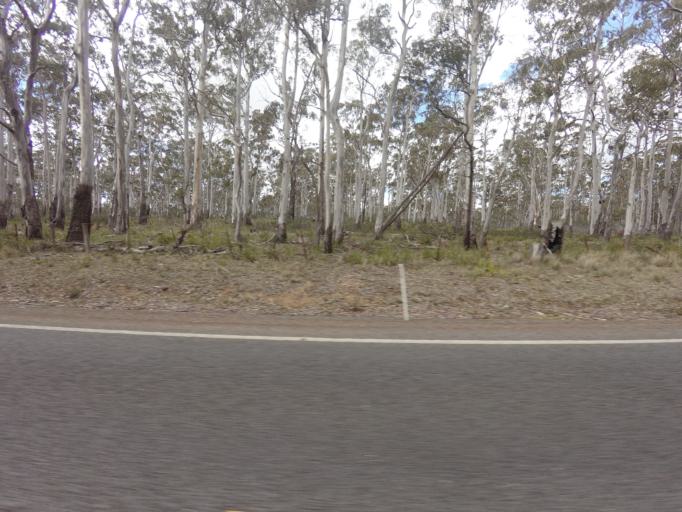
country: AU
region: Tasmania
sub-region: Northern Midlands
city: Evandale
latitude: -41.9714
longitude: 147.6480
